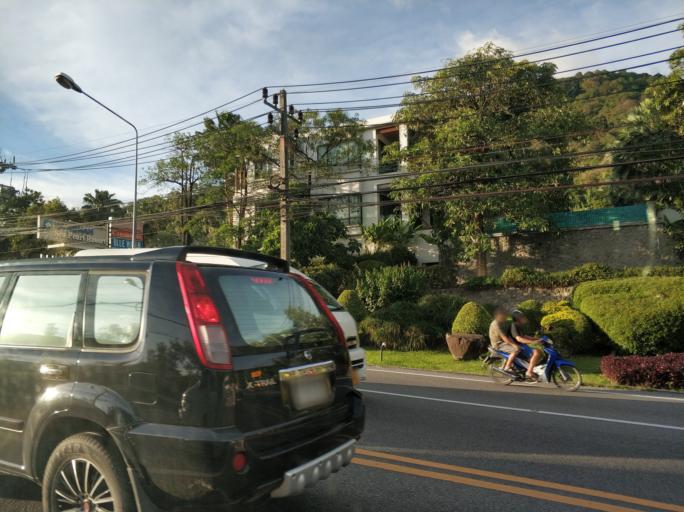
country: TH
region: Phuket
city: Patong
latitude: 7.9039
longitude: 98.3141
